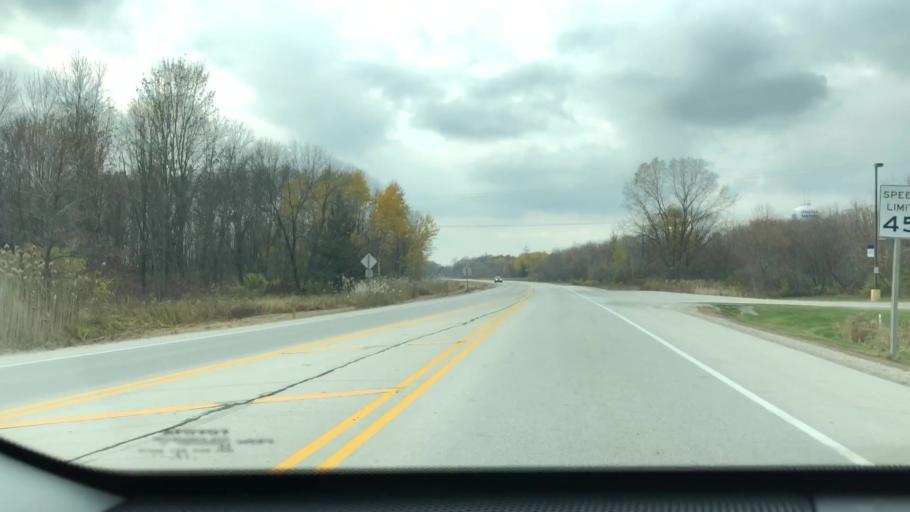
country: US
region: Wisconsin
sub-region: Brown County
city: Oneida
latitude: 44.5015
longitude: -88.1959
